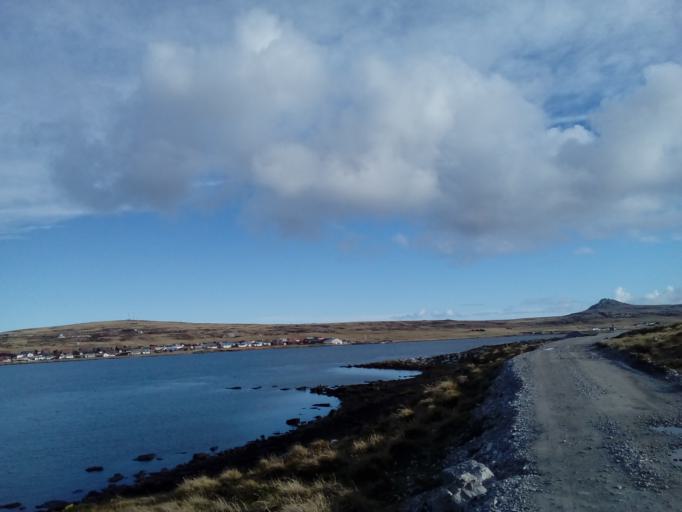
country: FK
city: Stanley
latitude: -51.6824
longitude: -57.8828
